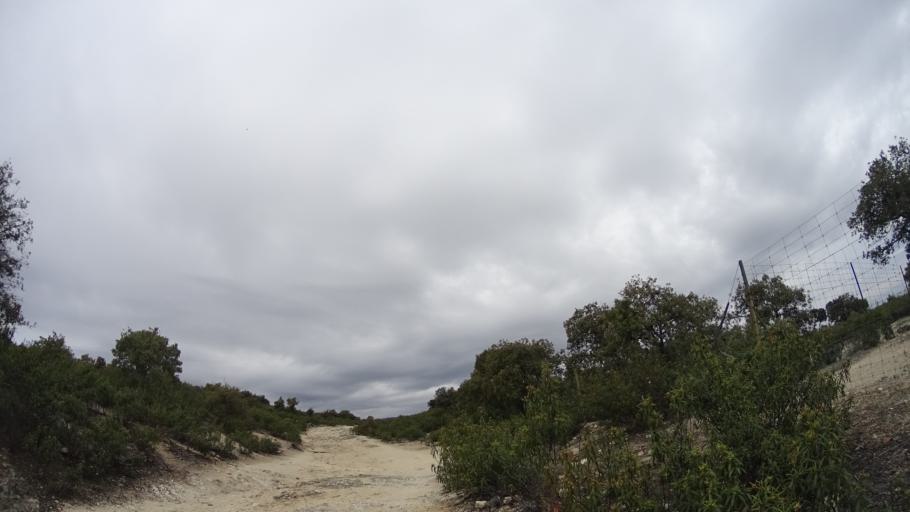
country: ES
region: Madrid
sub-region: Provincia de Madrid
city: Hoyo de Manzanares
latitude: 40.5945
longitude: -3.8851
